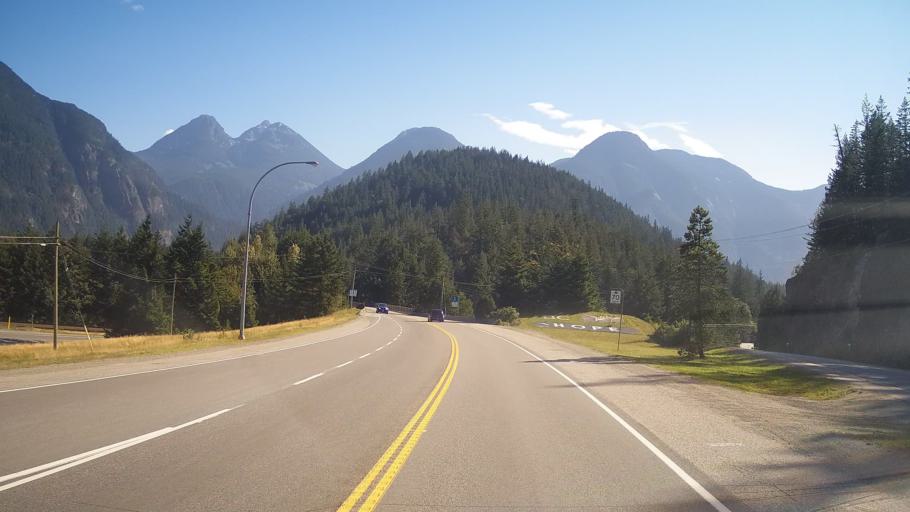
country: CA
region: British Columbia
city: Hope
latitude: 49.3921
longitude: -121.4602
